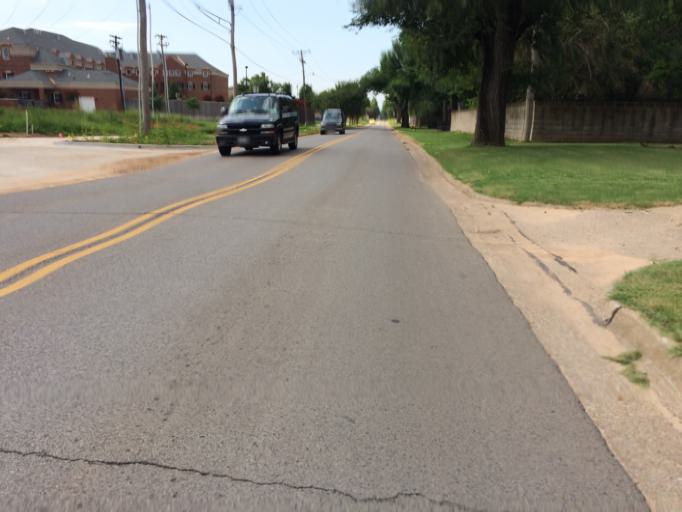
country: US
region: Oklahoma
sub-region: Cleveland County
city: Norman
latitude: 35.2016
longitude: -97.4502
